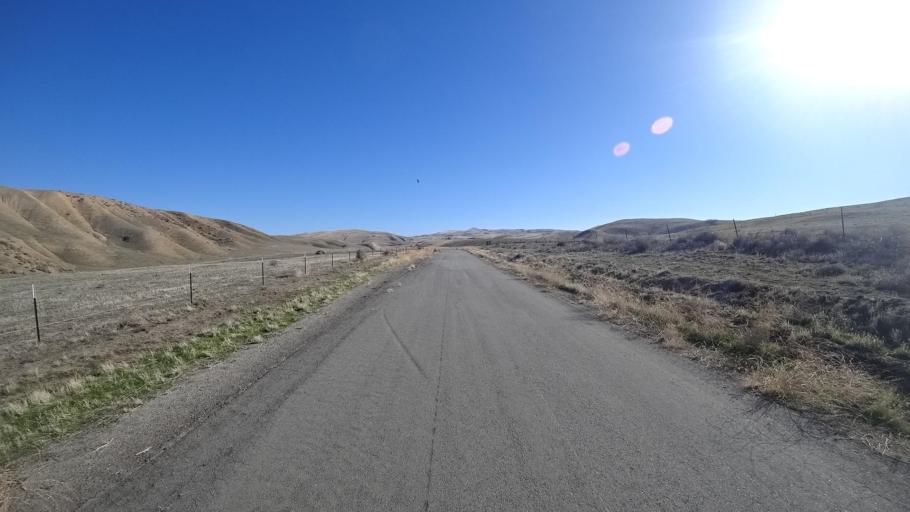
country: US
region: California
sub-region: Kern County
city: Maricopa
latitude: 34.9730
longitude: -119.4585
